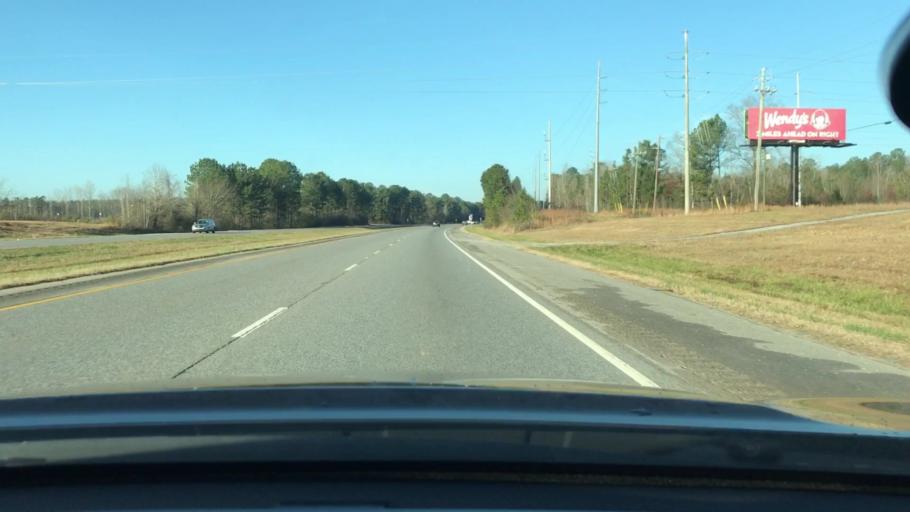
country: US
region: Alabama
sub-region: Shelby County
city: Westover
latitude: 33.3485
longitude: -86.5666
